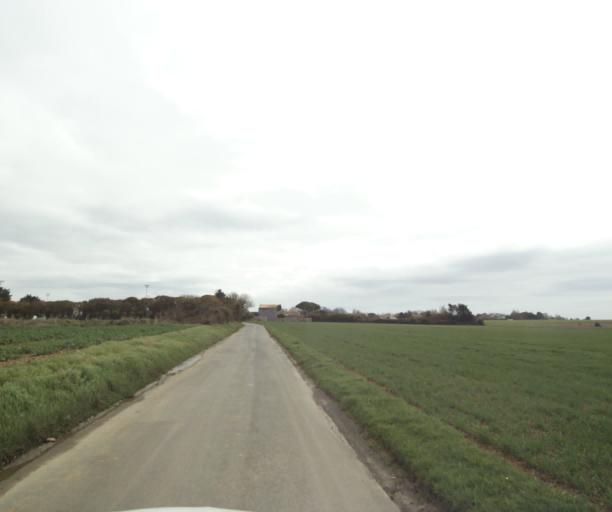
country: FR
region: Poitou-Charentes
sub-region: Departement de la Charente-Maritime
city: Nieul-sur-Mer
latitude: 46.1901
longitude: -1.1718
